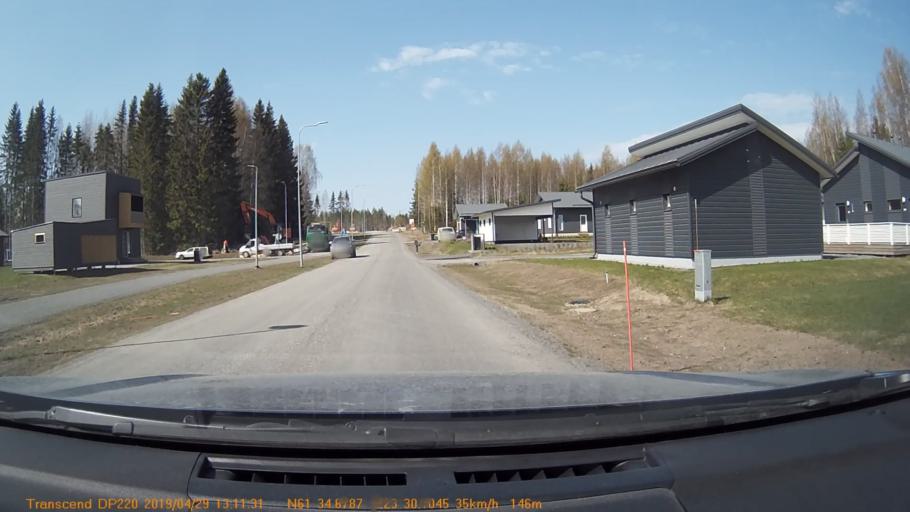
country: FI
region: Pirkanmaa
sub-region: Tampere
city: Yloejaervi
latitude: 61.5780
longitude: 23.5016
